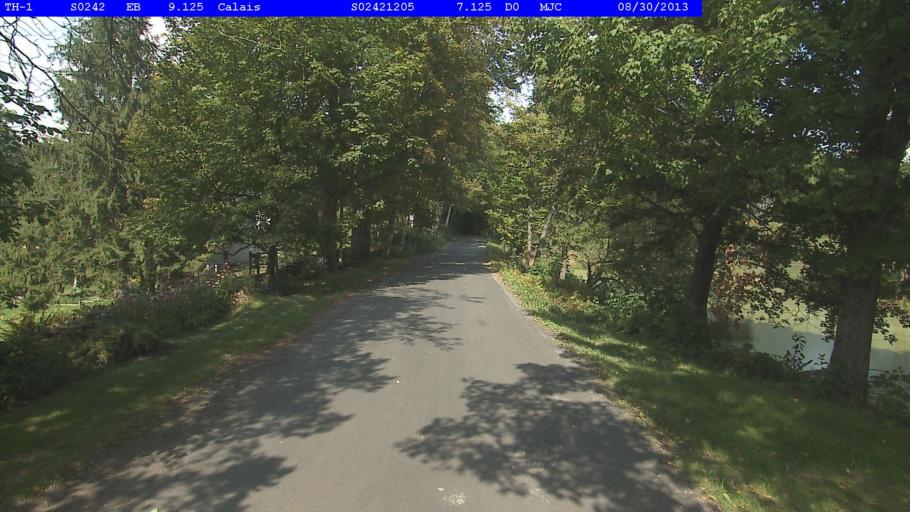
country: US
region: Vermont
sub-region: Caledonia County
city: Hardwick
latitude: 44.4007
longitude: -72.4342
